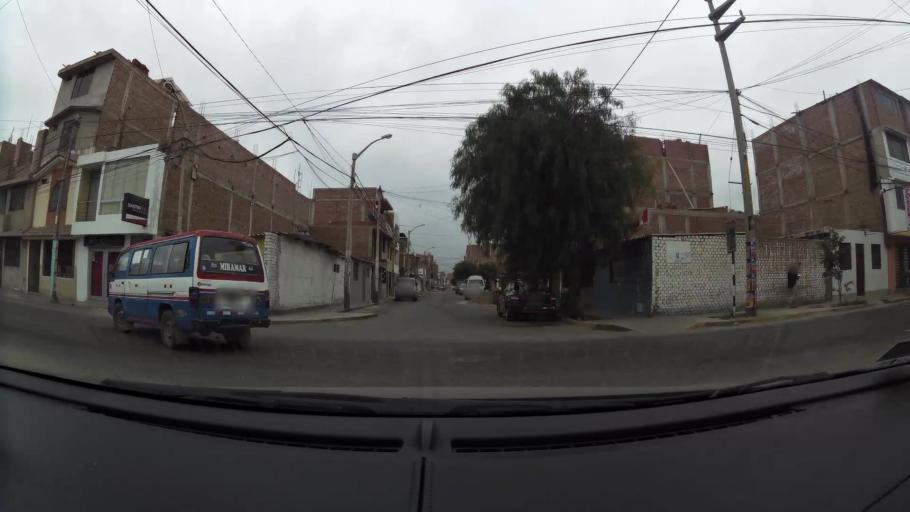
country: PE
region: La Libertad
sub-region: Provincia de Trujillo
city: Trujillo
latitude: -8.1234
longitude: -79.0276
